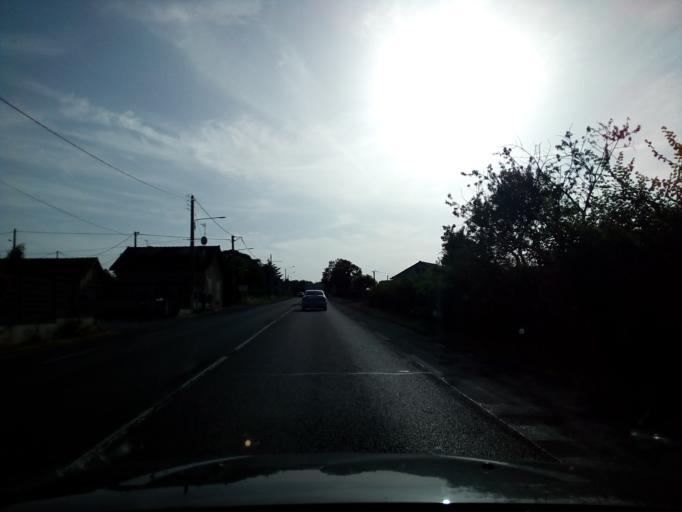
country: FR
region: Auvergne
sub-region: Departement de l'Allier
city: Premilhat
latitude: 46.3376
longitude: 2.5545
